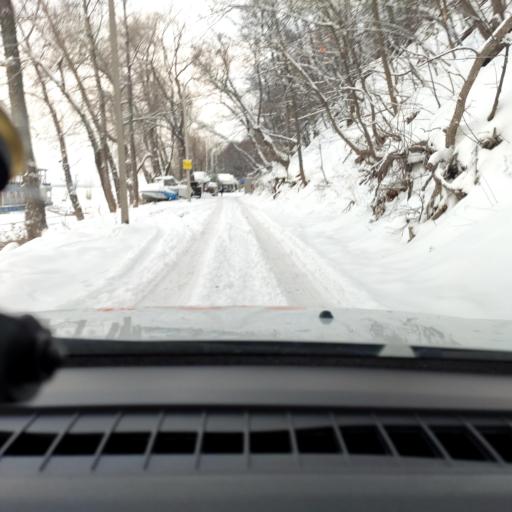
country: RU
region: Samara
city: Samara
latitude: 53.2925
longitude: 50.1923
